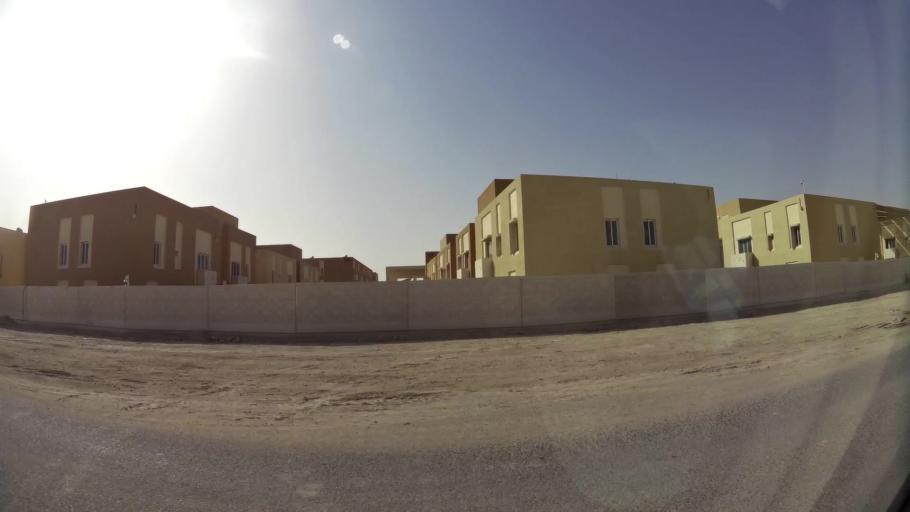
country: QA
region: Baladiyat ar Rayyan
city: Ar Rayyan
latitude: 25.3330
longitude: 51.4209
